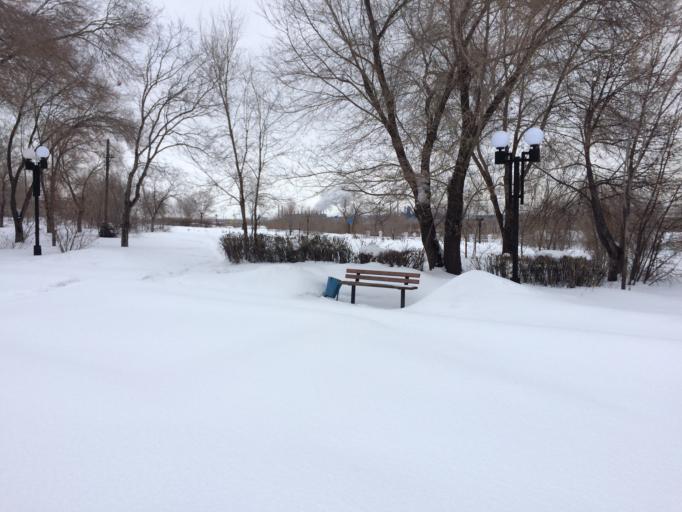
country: RU
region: Chelyabinsk
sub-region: Gorod Magnitogorsk
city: Magnitogorsk
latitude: 53.4164
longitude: 59.0019
